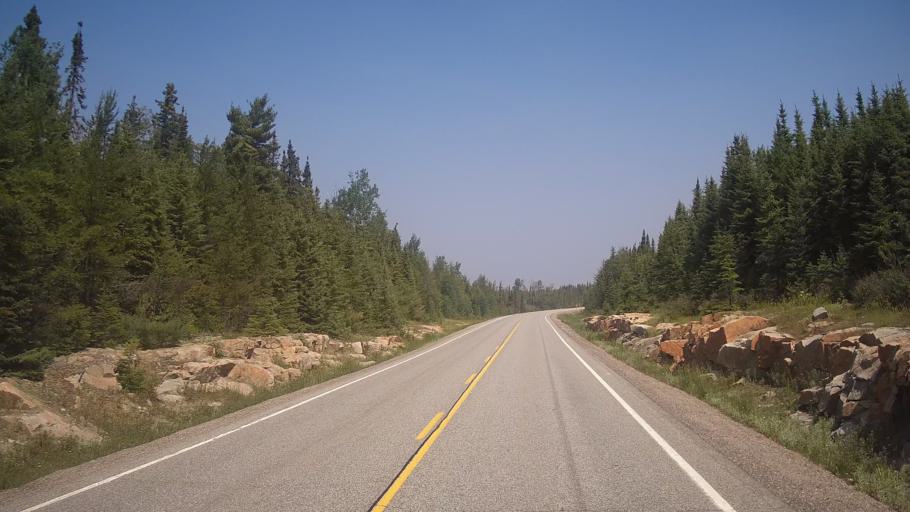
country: CA
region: Ontario
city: Timmins
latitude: 48.1879
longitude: -81.5835
